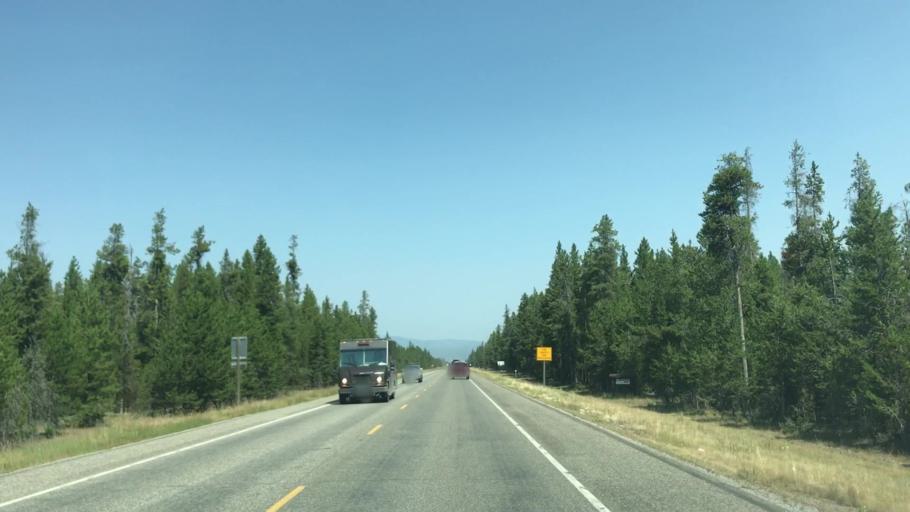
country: US
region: Montana
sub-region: Gallatin County
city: West Yellowstone
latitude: 44.6776
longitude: -111.1006
